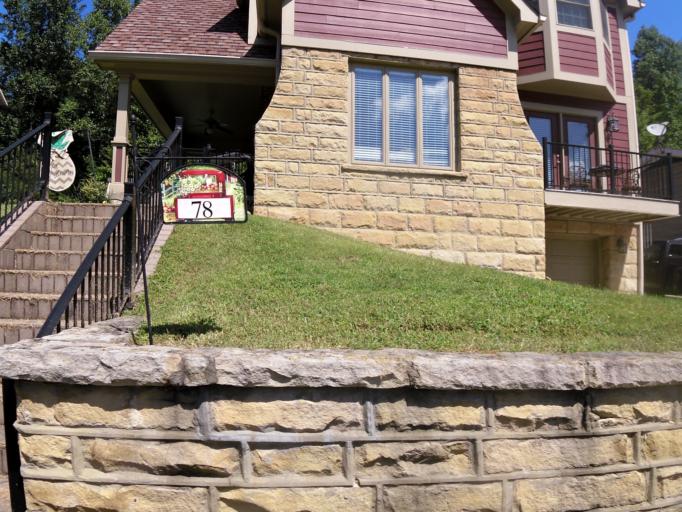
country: US
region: Kentucky
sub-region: Leslie County
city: Hyden
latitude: 37.1644
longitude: -83.3757
